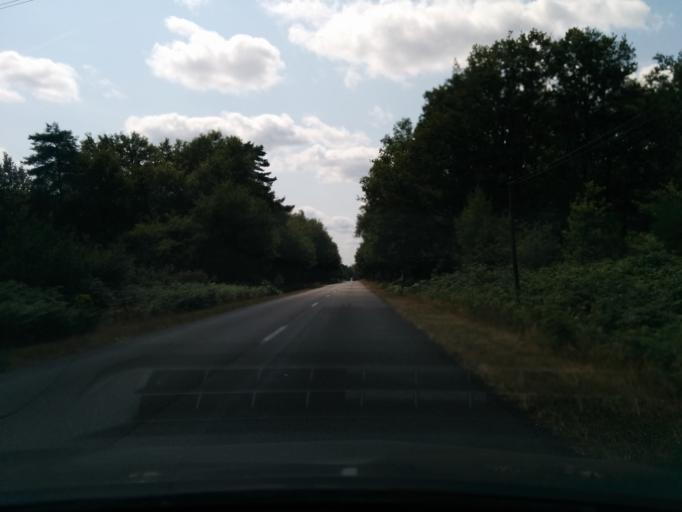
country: FR
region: Centre
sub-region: Departement du Cher
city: Neuvy-sur-Barangeon
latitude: 47.3228
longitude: 2.3018
